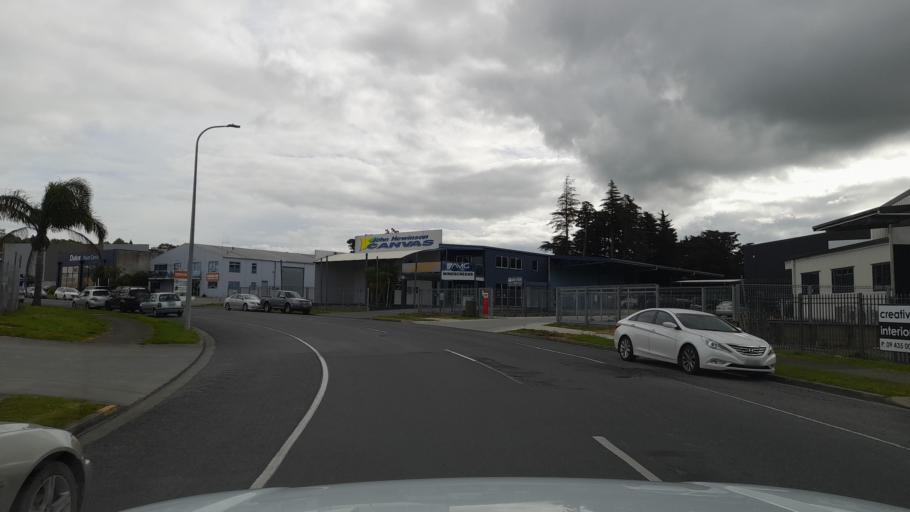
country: NZ
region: Northland
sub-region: Whangarei
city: Whangarei
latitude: -35.7500
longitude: 174.3123
